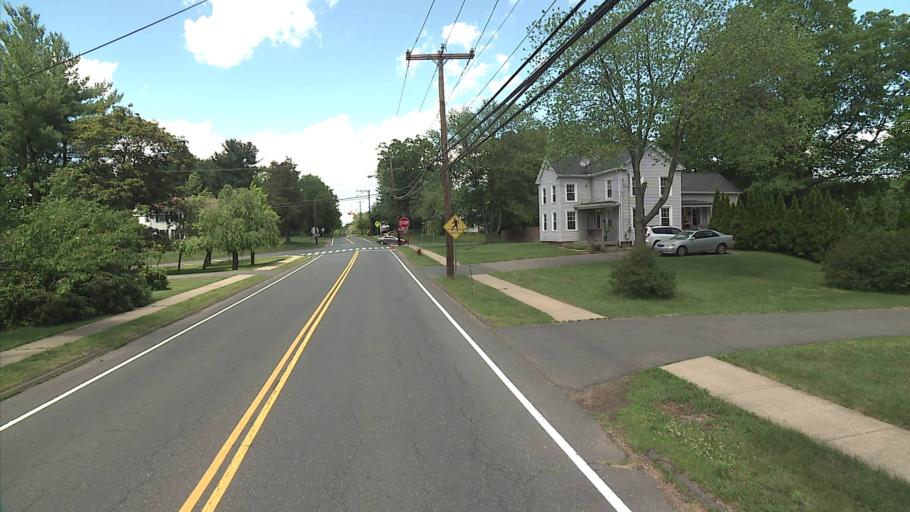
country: US
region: Connecticut
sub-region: Hartford County
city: Hazardville
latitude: 41.9907
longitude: -72.5394
